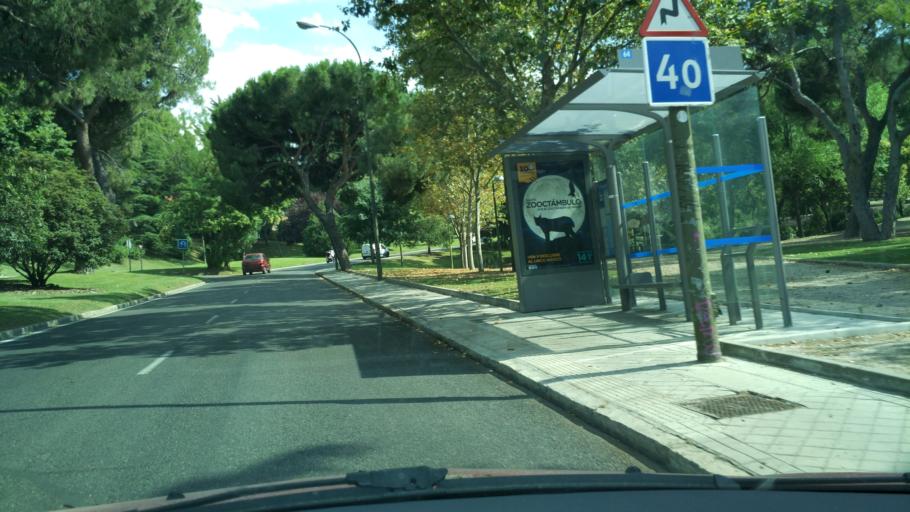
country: ES
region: Madrid
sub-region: Provincia de Madrid
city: Tetuan de las Victorias
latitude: 40.4621
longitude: -3.7194
